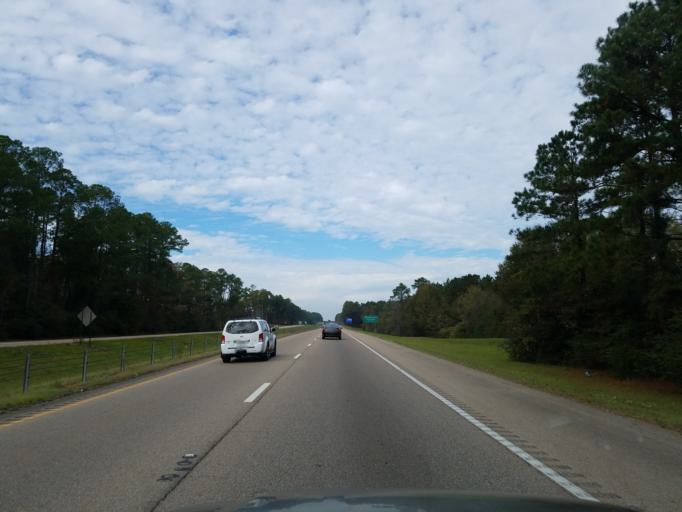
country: US
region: Mississippi
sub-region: Lamar County
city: West Hattiesburg
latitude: 31.2513
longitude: -89.3310
